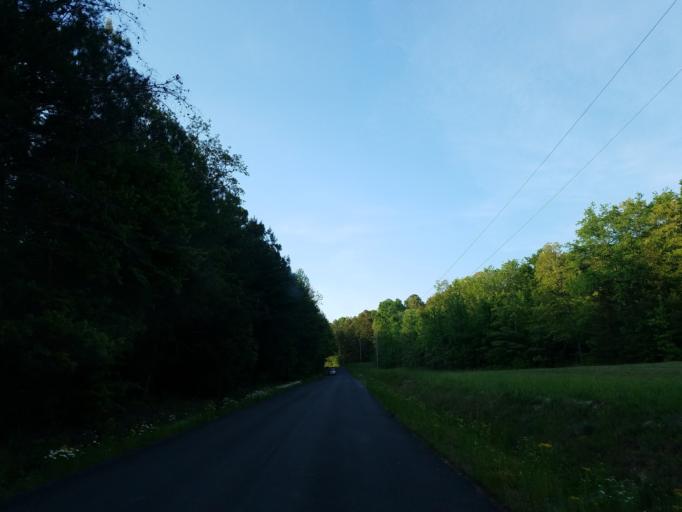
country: US
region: Georgia
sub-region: Whitfield County
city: Dalton
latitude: 34.6524
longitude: -85.0830
